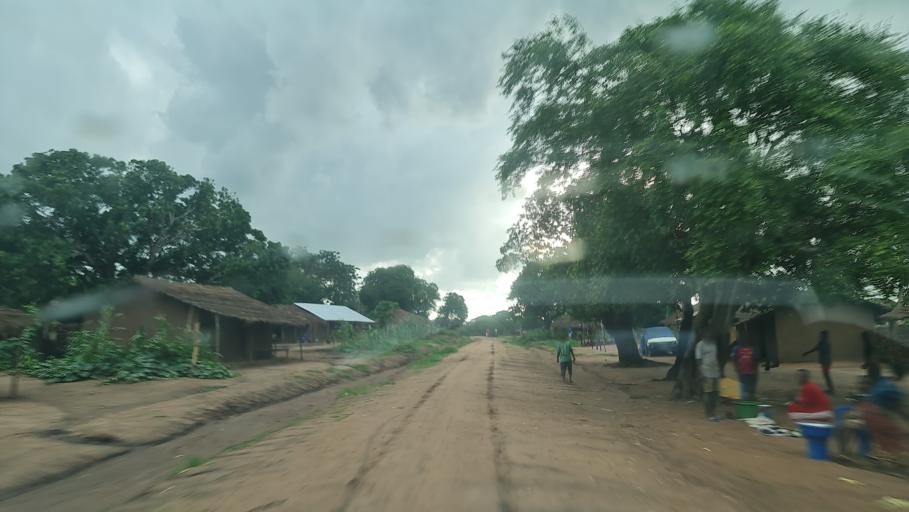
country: MZ
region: Nampula
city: Nacala
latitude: -13.9902
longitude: 40.3726
